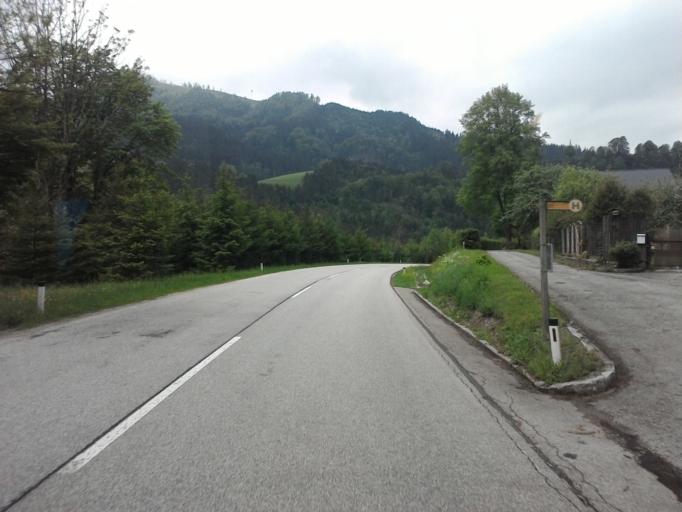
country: AT
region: Styria
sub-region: Politischer Bezirk Liezen
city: Landl
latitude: 47.6965
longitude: 14.6856
